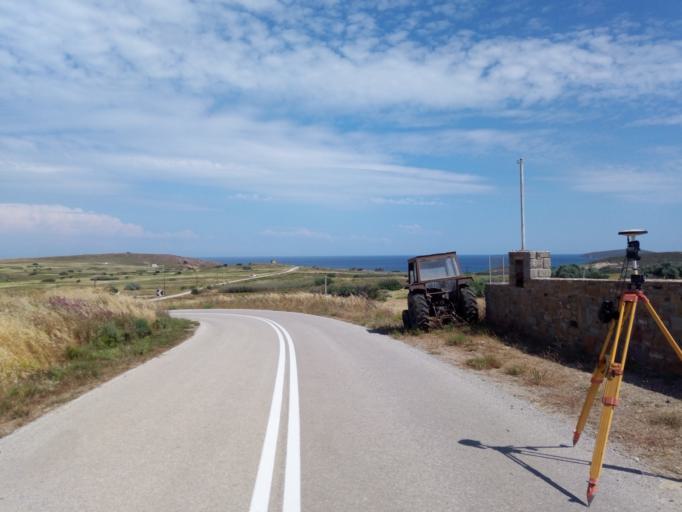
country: GR
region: North Aegean
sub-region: Nomos Lesvou
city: Myrina
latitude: 39.8592
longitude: 25.3308
